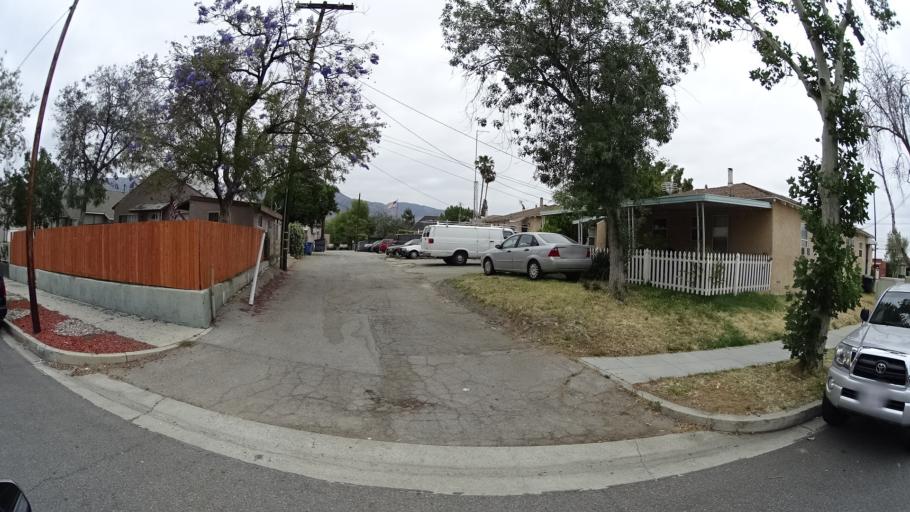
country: US
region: California
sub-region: Los Angeles County
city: Burbank
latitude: 34.1835
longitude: -118.3252
